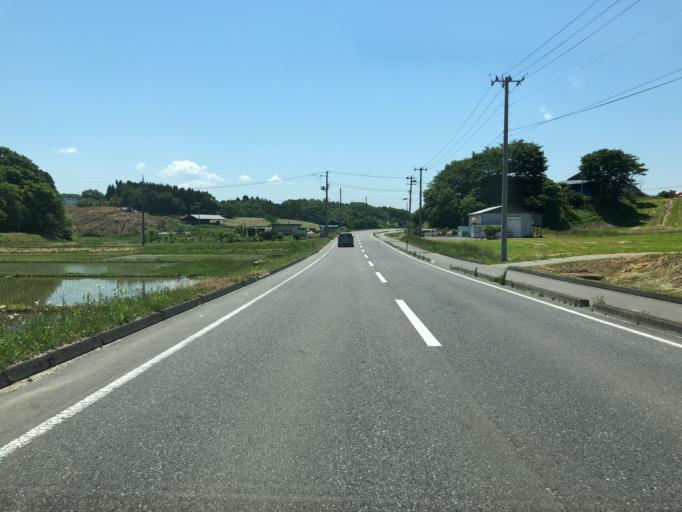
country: JP
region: Fukushima
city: Motomiya
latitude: 37.5114
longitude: 140.4589
